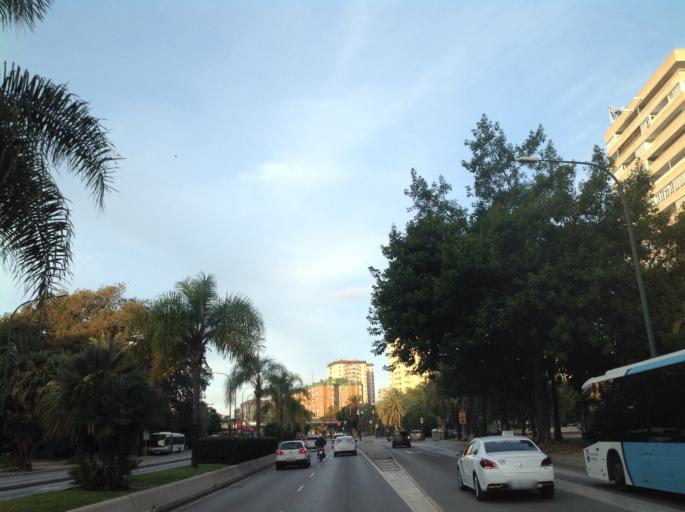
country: ES
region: Andalusia
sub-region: Provincia de Malaga
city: Malaga
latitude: 36.7172
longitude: -4.4339
